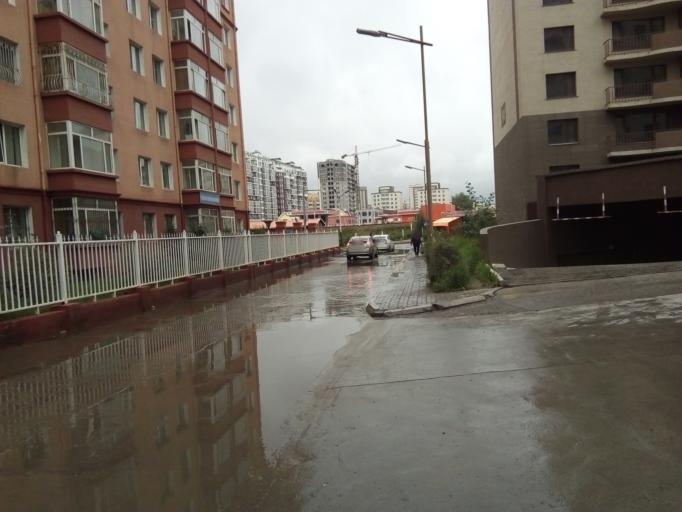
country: MN
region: Ulaanbaatar
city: Ulaanbaatar
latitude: 47.9066
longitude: 106.9357
